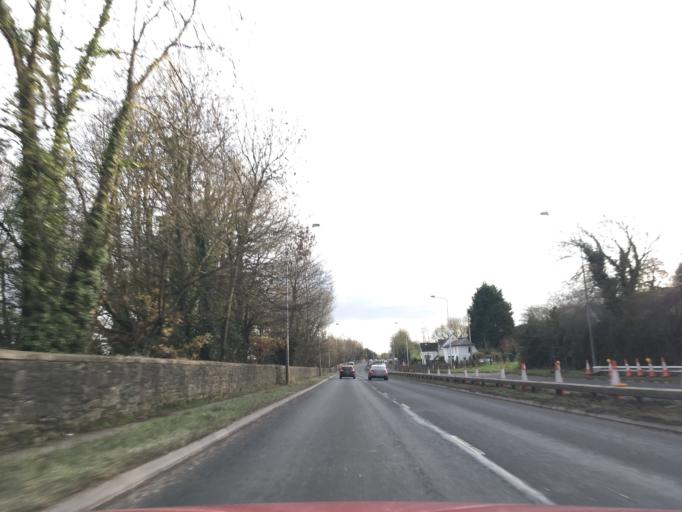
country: GB
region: Wales
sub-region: Newport
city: Newport
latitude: 51.5731
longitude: -3.0410
